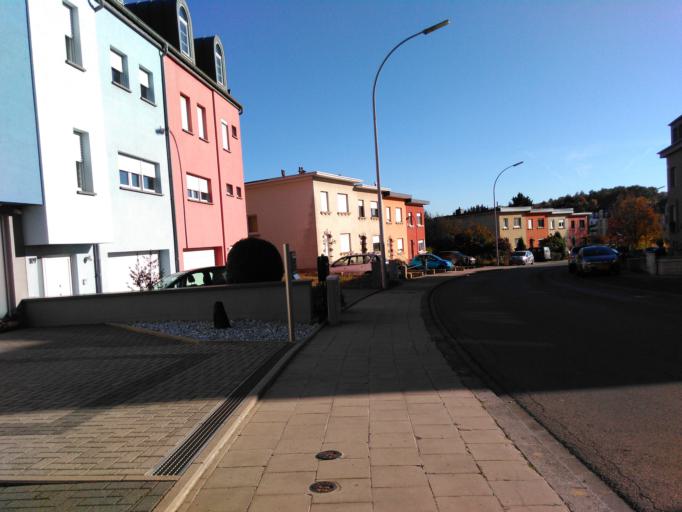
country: LU
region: Luxembourg
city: Belvaux
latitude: 49.5055
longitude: 5.9308
